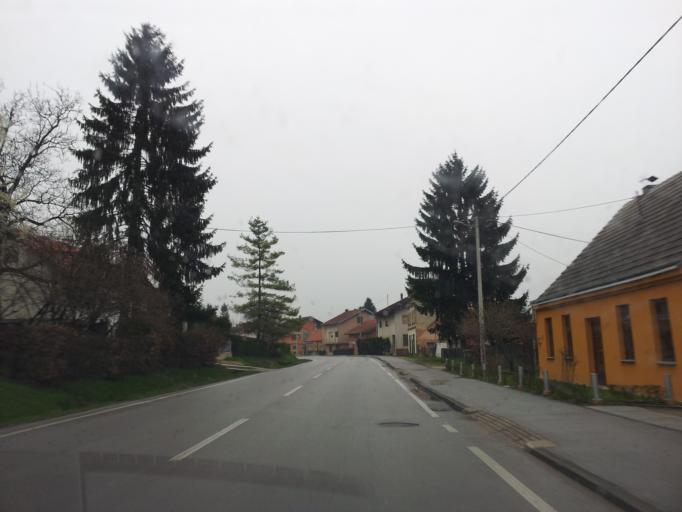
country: HR
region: Karlovacka
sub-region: Grad Karlovac
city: Karlovac
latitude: 45.4726
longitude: 15.5598
